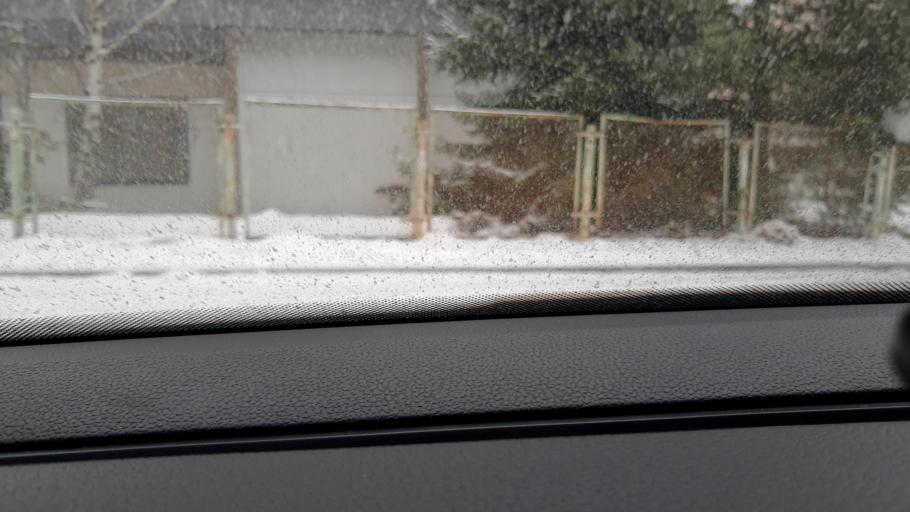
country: RU
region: Moskovskaya
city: Nemchinovka
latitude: 55.7545
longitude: 37.3777
